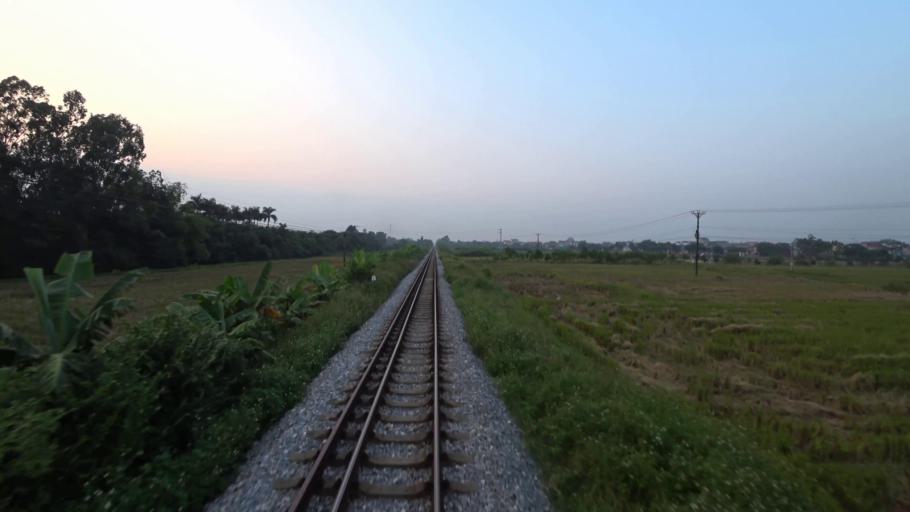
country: VN
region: Ha Noi
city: Dong Anh
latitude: 21.1327
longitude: 105.8737
